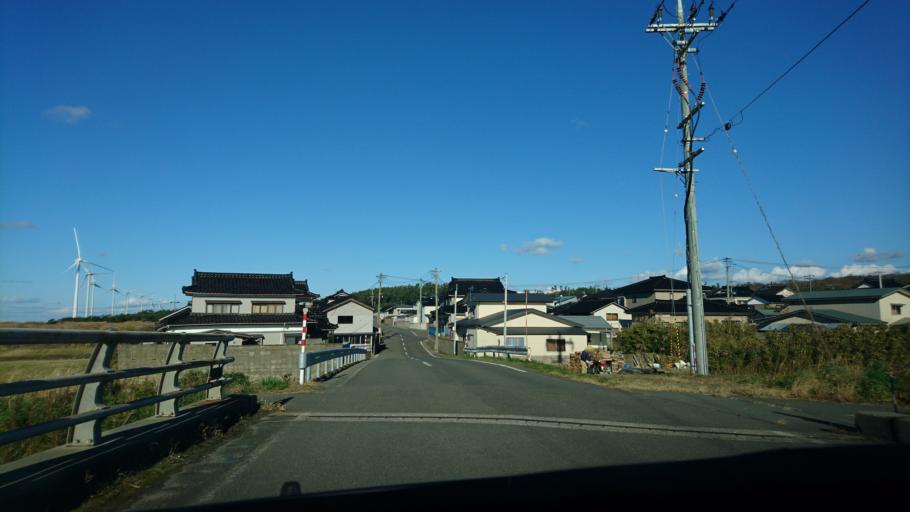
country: JP
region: Yamagata
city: Yuza
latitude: 39.3667
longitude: 140.0111
